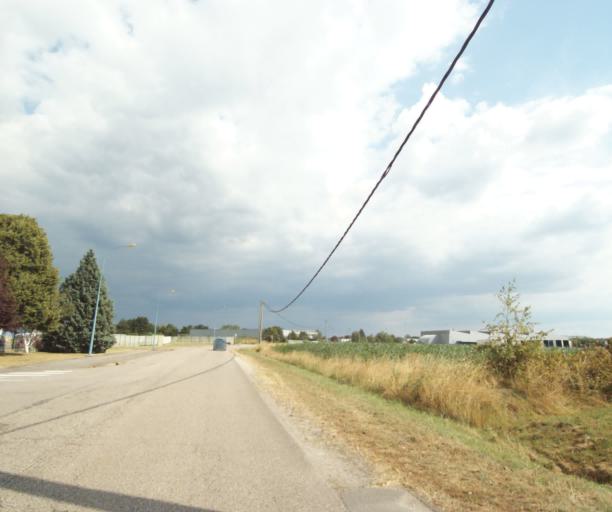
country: FR
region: Lorraine
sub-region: Departement de Meurthe-et-Moselle
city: Chanteheux
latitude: 48.5859
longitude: 6.5236
